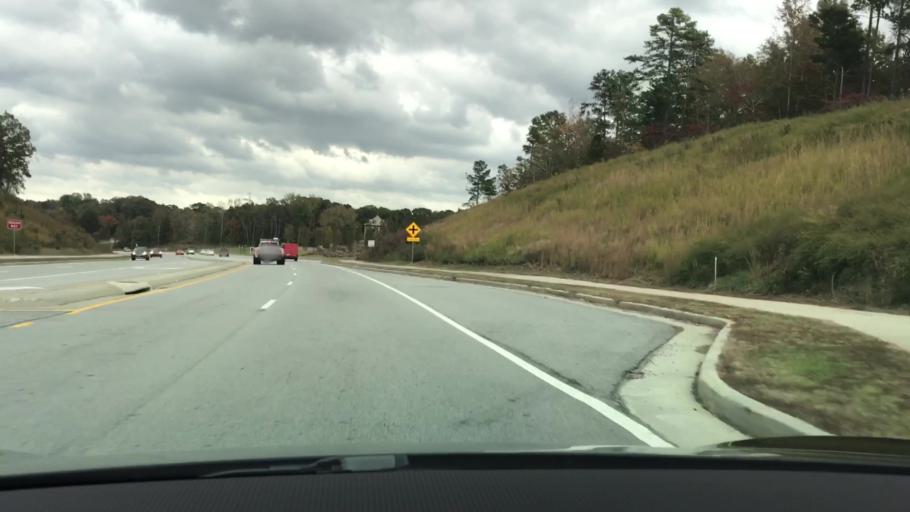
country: US
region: Georgia
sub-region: Hall County
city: Flowery Branch
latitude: 34.1100
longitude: -83.8639
